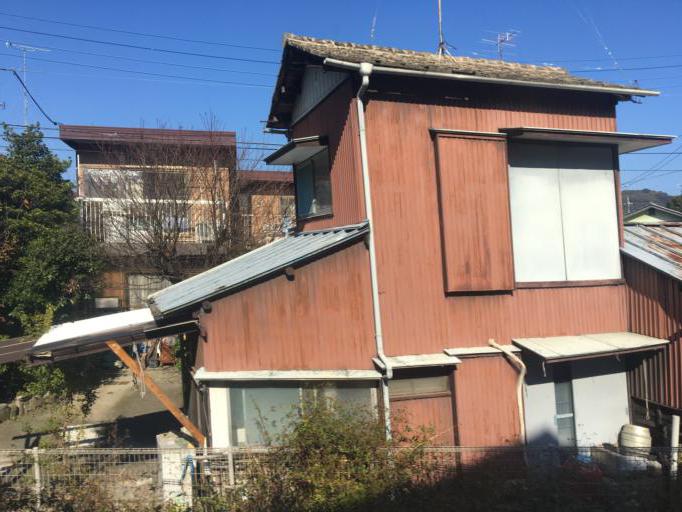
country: JP
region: Tochigi
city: Ashikaga
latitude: 36.3358
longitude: 139.4392
